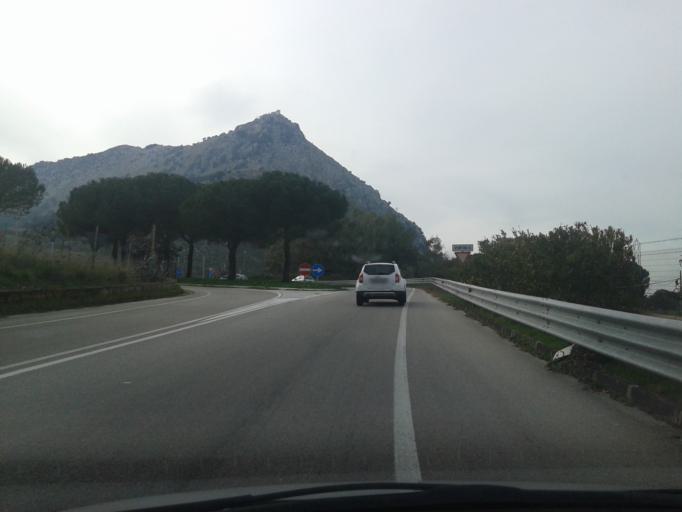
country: IT
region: Sicily
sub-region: Palermo
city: Giacalone
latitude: 38.0274
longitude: 13.2424
